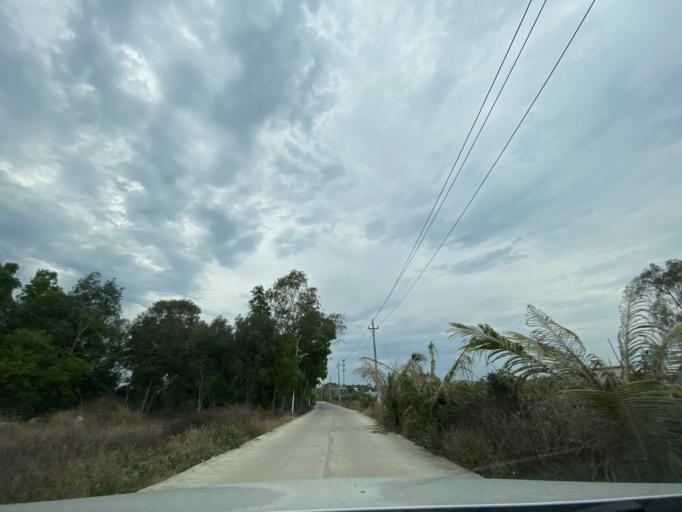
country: CN
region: Hainan
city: Yingzhou
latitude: 18.4113
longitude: 109.8210
